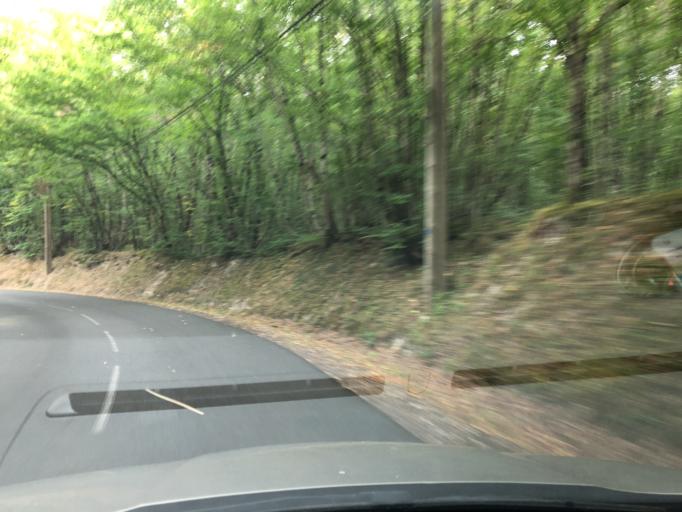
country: FR
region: Centre
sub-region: Departement d'Indre-et-Loire
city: Mazieres-de-Touraine
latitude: 47.3905
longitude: 0.4497
